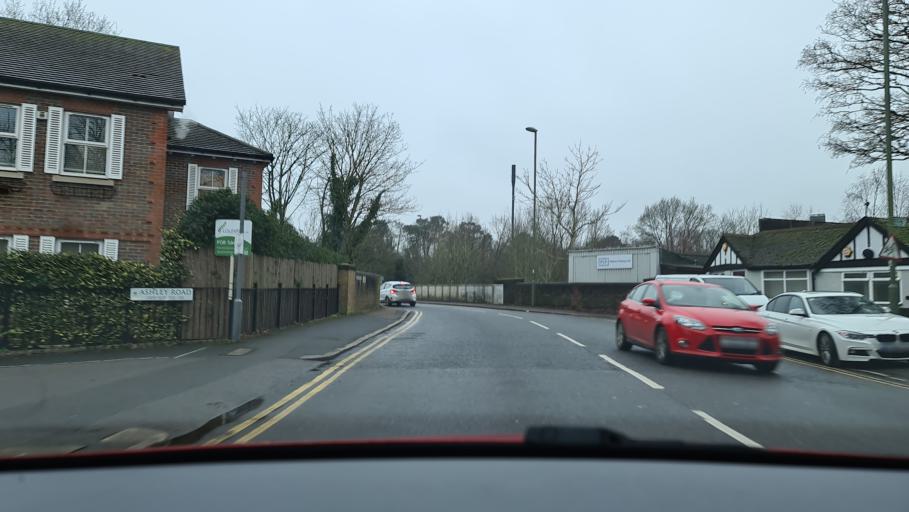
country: GB
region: England
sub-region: Surrey
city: Walton-on-Thames
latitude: 51.3717
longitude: -0.4236
